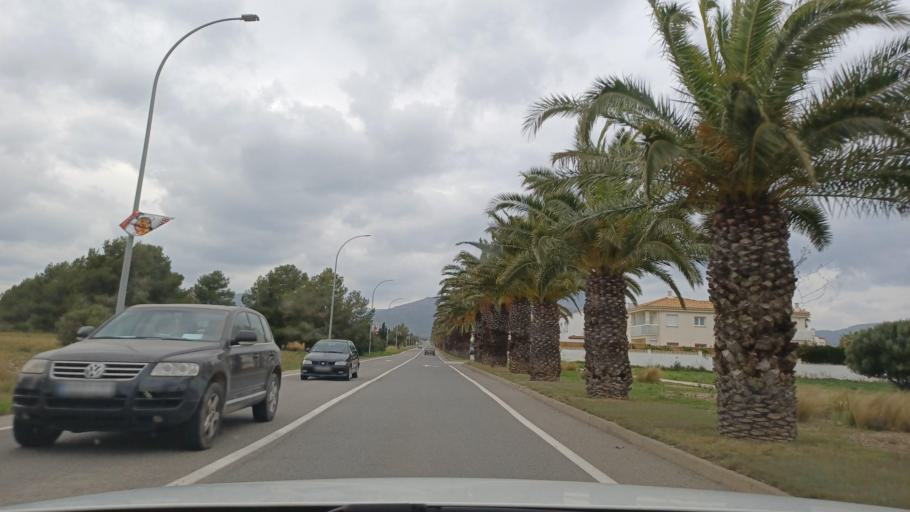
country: ES
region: Catalonia
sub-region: Provincia de Tarragona
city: Colldejou
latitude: 41.0194
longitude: 0.9390
